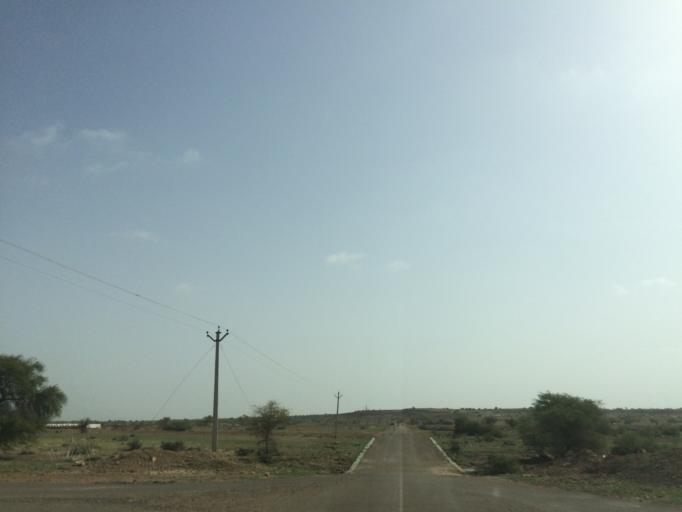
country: IN
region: Rajasthan
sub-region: Jaisalmer
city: Jaisalmer
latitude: 26.8391
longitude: 70.7458
